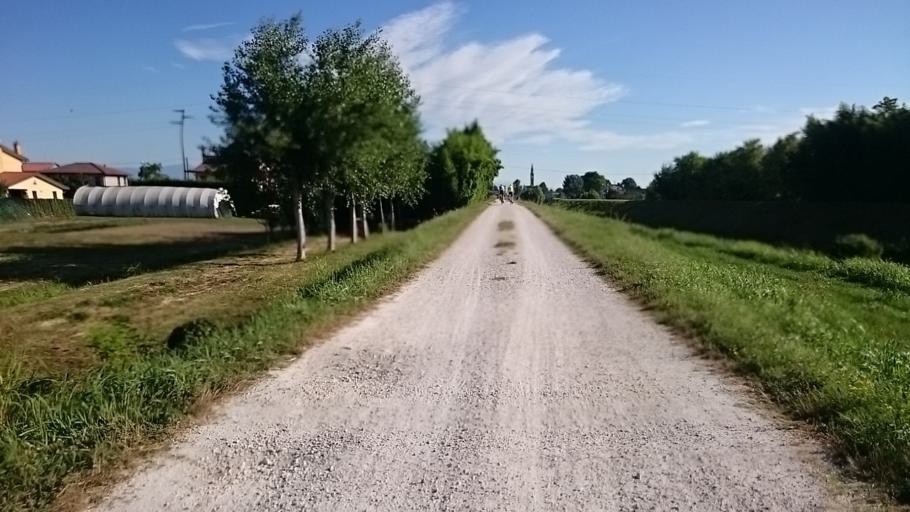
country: IT
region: Veneto
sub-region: Provincia di Padova
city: Campodarsego
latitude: 45.4904
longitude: 11.9022
